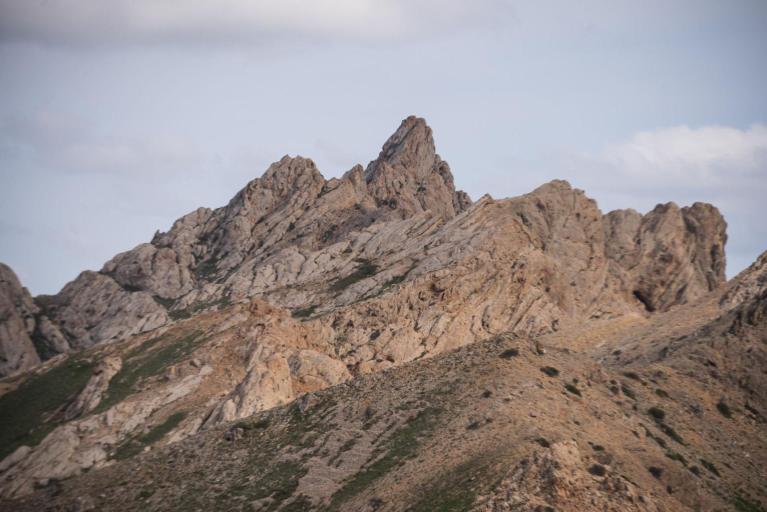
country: KZ
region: Ongtustik Qazaqstan
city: Ashchysay
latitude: 43.7500
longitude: 68.8242
